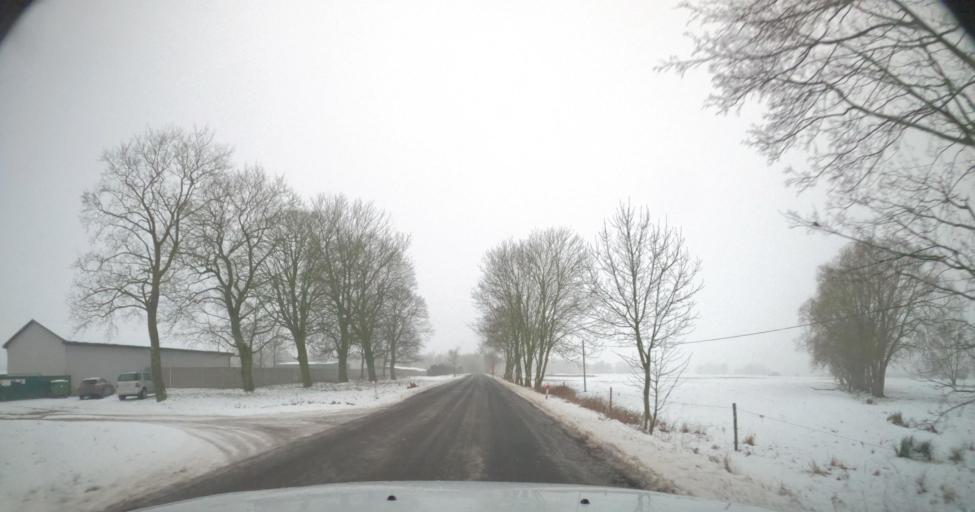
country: PL
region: West Pomeranian Voivodeship
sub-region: Powiat goleniowski
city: Goleniow
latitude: 53.5742
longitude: 14.7257
